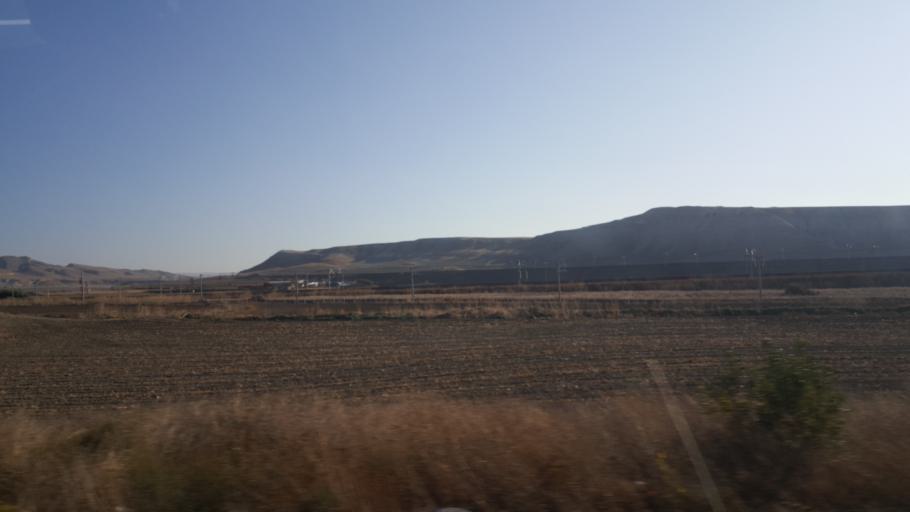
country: TR
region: Ankara
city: Polatli
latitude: 39.5749
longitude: 32.0115
